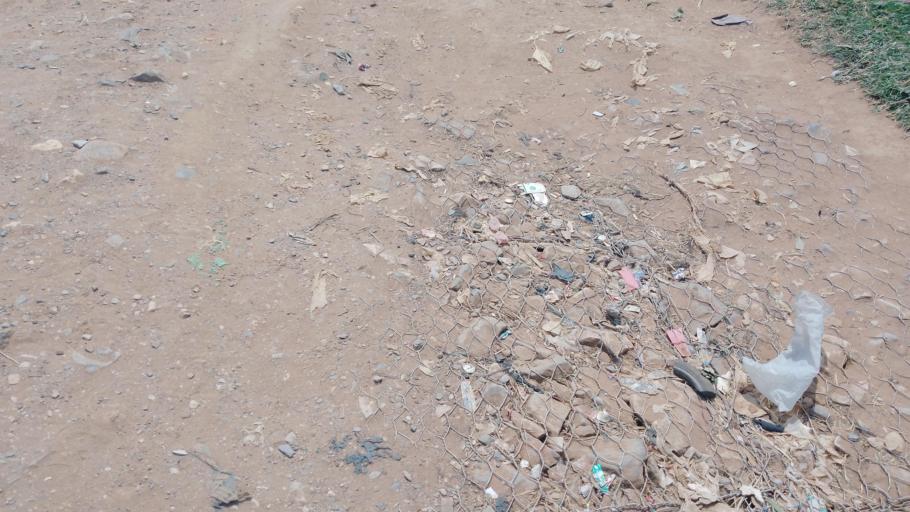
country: ZM
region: Lusaka
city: Lusaka
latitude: -15.3934
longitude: 28.3767
